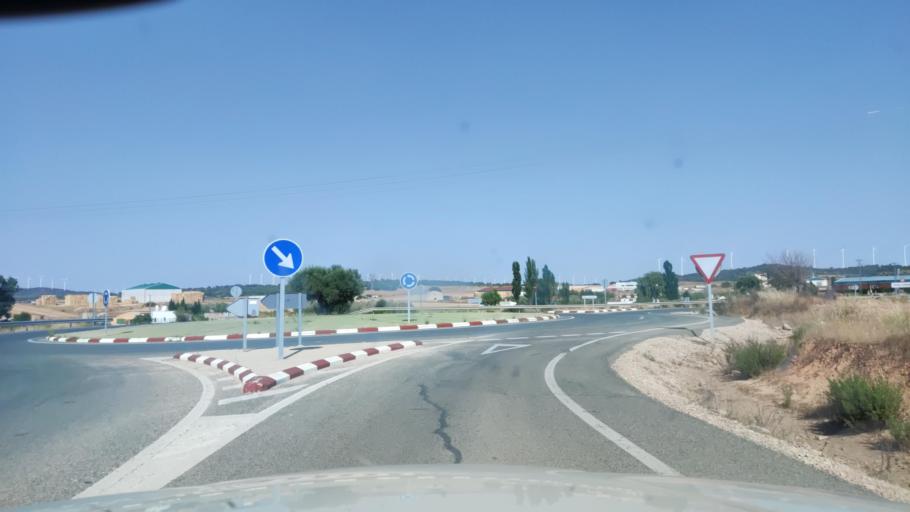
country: ES
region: Castille-La Mancha
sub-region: Provincia de Albacete
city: Pozo-Canada
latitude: 38.8104
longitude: -1.7387
